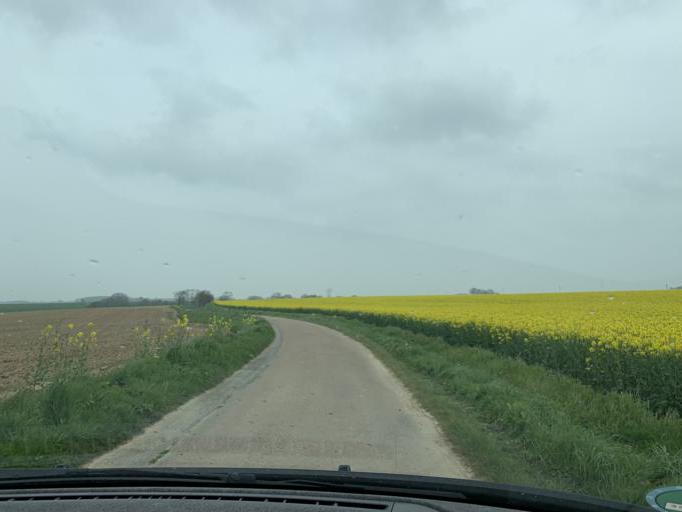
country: FR
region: Haute-Normandie
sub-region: Departement de la Seine-Maritime
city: Fontaine-le-Dun
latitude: 49.8564
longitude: 0.8119
